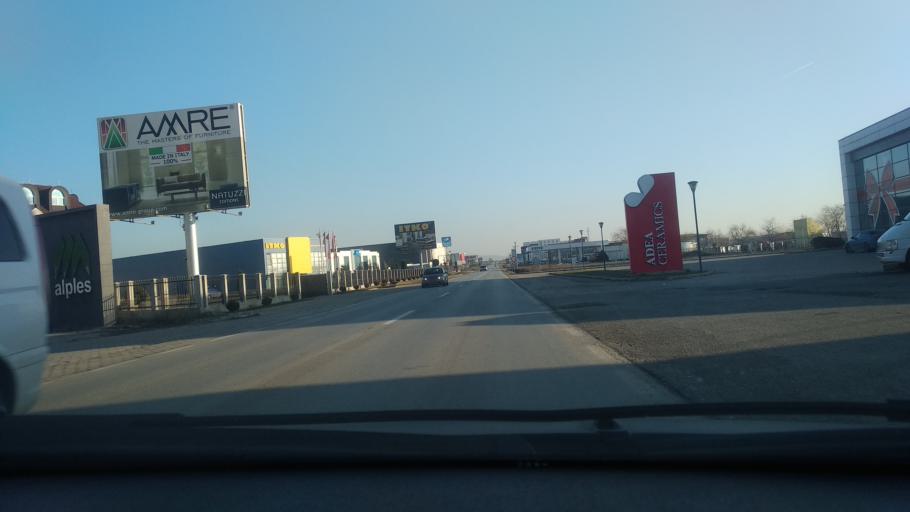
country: XK
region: Pristina
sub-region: Lipjan
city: Lipljan
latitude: 42.5597
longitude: 21.1358
